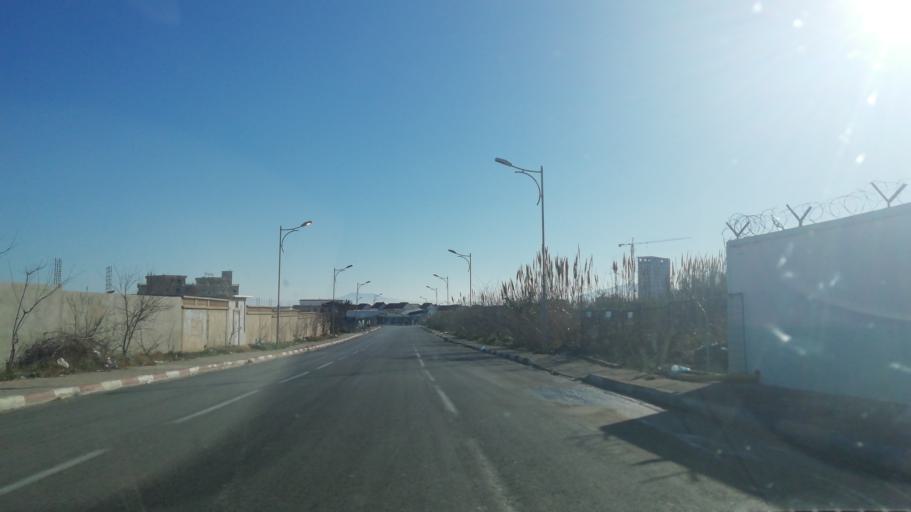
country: DZ
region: Oran
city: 'Ain el Turk
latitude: 35.7581
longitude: -0.7940
